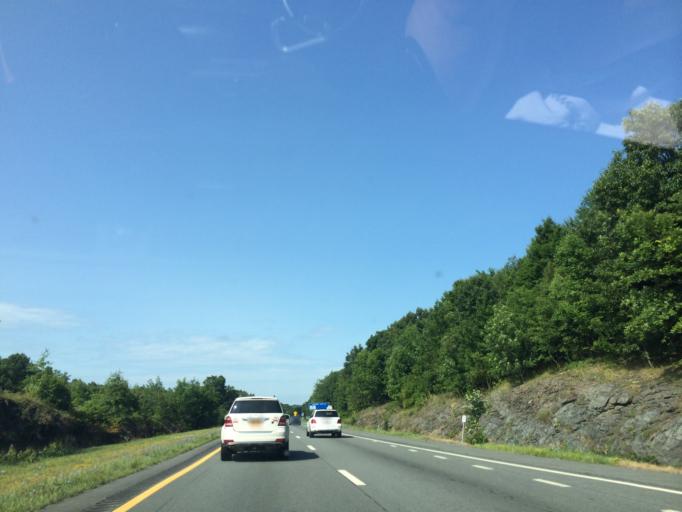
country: US
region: New York
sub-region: Orange County
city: Orange Lake
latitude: 41.5177
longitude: -74.1150
